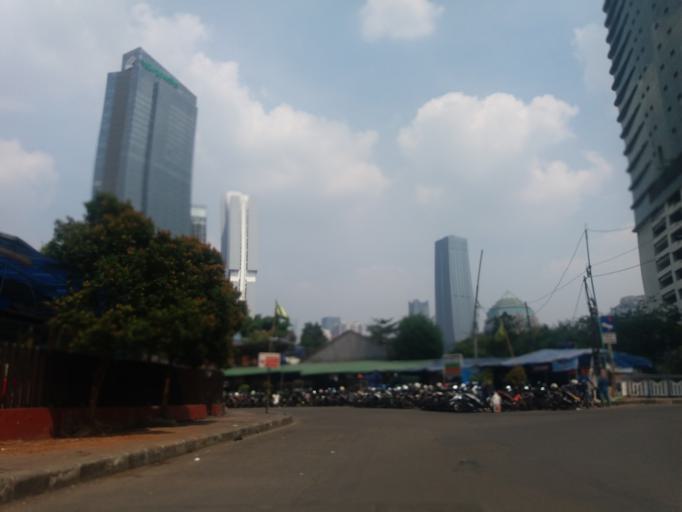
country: ID
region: Jakarta Raya
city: Jakarta
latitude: -6.2183
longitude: 106.8177
